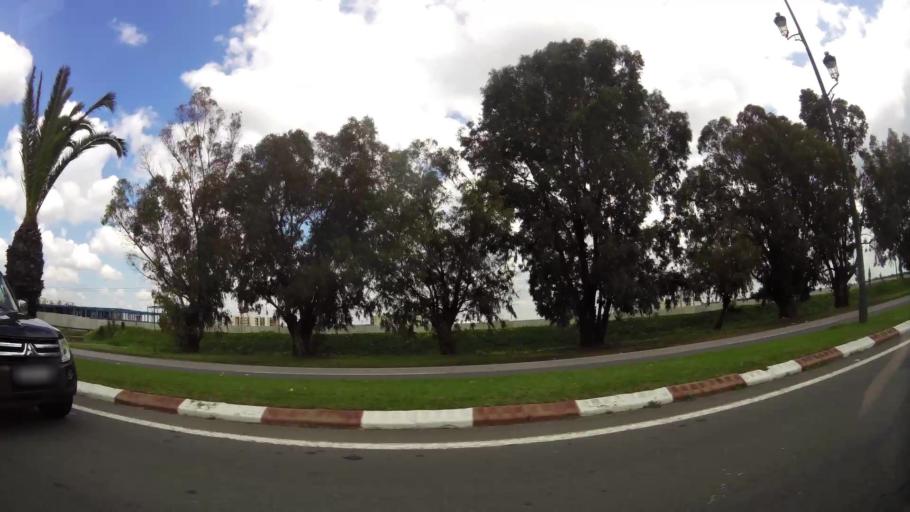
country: MA
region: Chaouia-Ouardigha
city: Nouaseur
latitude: 33.3868
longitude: -7.5653
